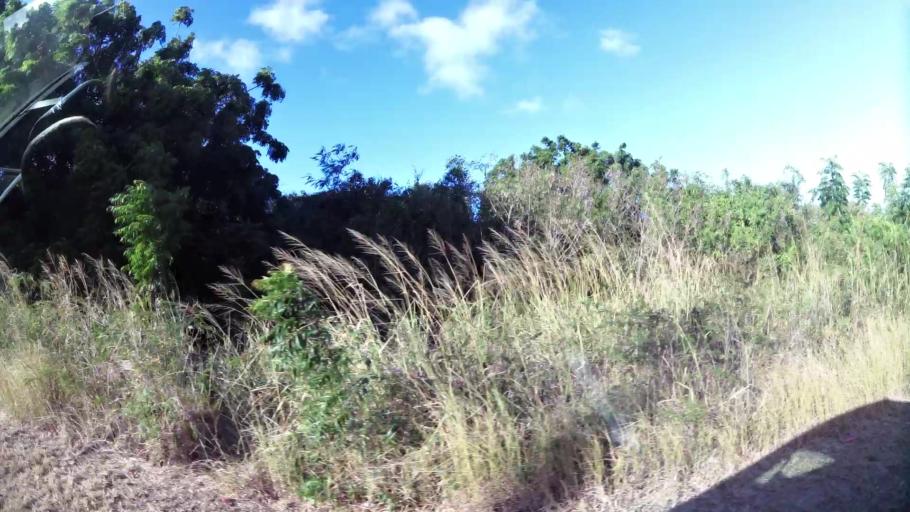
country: AG
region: Saint George
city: Piggotts
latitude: 17.1292
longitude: -61.7918
